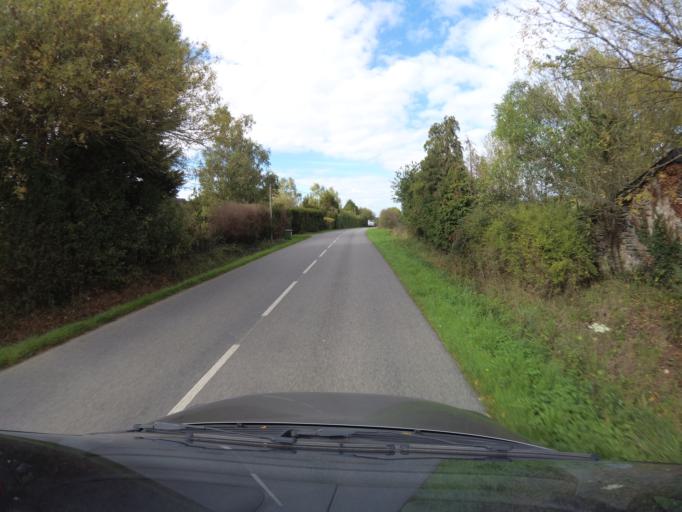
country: FR
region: Pays de la Loire
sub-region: Departement de la Loire-Atlantique
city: Bouvron
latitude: 47.4687
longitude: -1.8369
